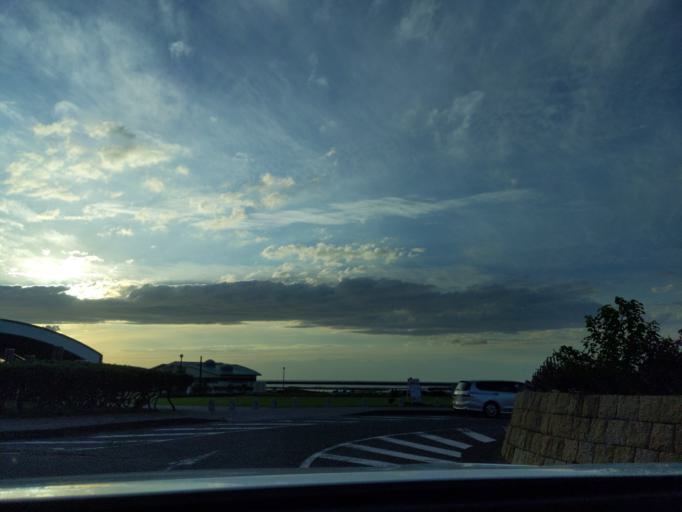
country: JP
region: Niigata
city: Kashiwazaki
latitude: 37.3708
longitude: 138.5467
